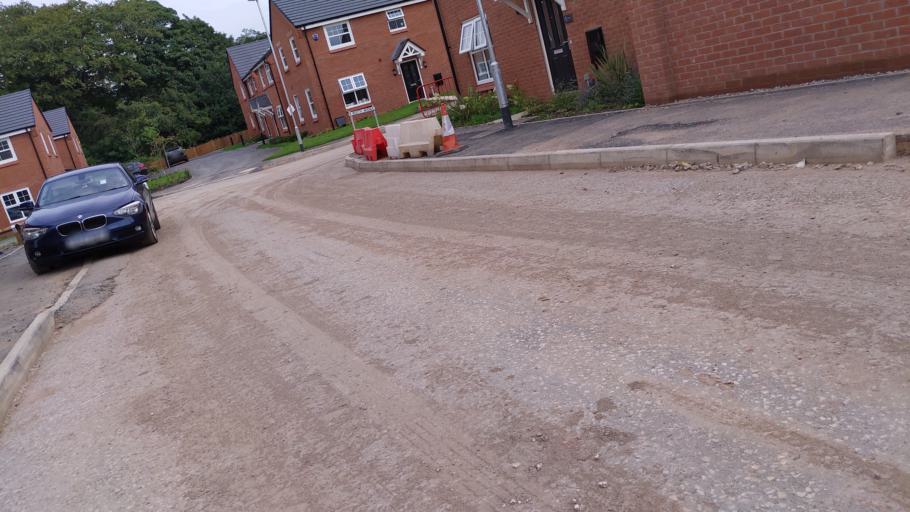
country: GB
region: England
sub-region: Lancashire
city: Coppull
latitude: 53.6309
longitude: -2.6419
